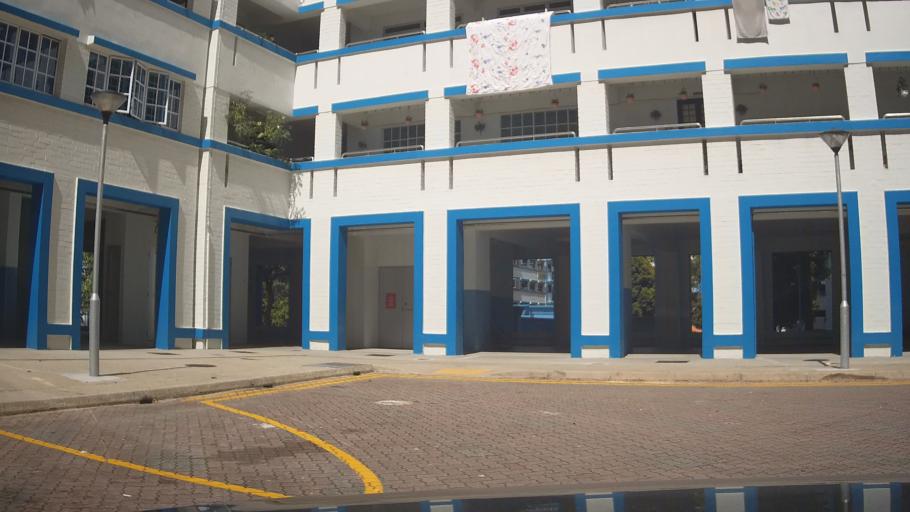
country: SG
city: Singapore
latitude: 1.3654
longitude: 103.9600
